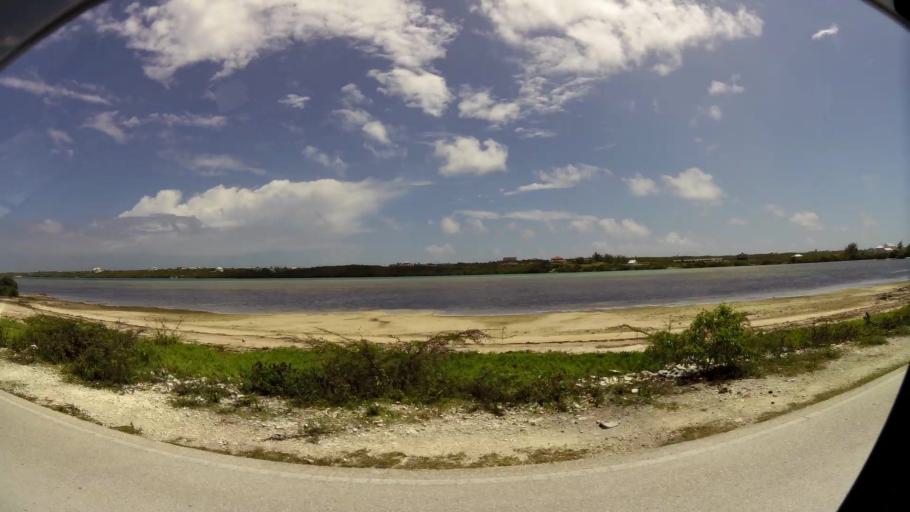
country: TC
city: Cockburn Town
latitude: 21.4843
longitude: -71.1422
